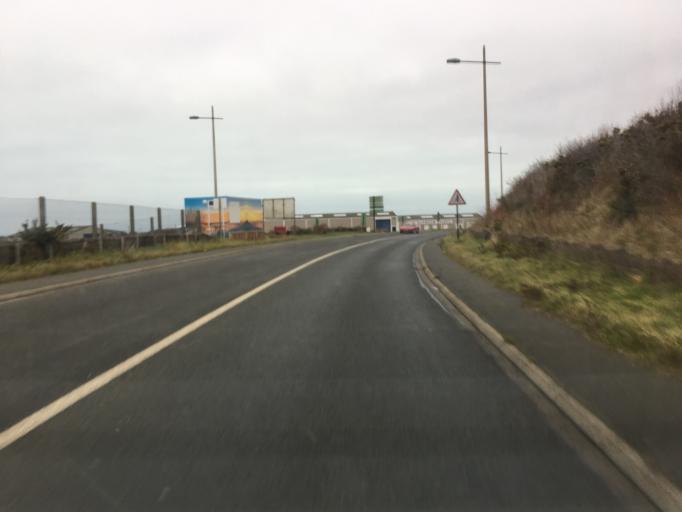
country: FR
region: Nord-Pas-de-Calais
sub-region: Departement du Pas-de-Calais
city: Le Portel
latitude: 50.6911
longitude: 1.5775
